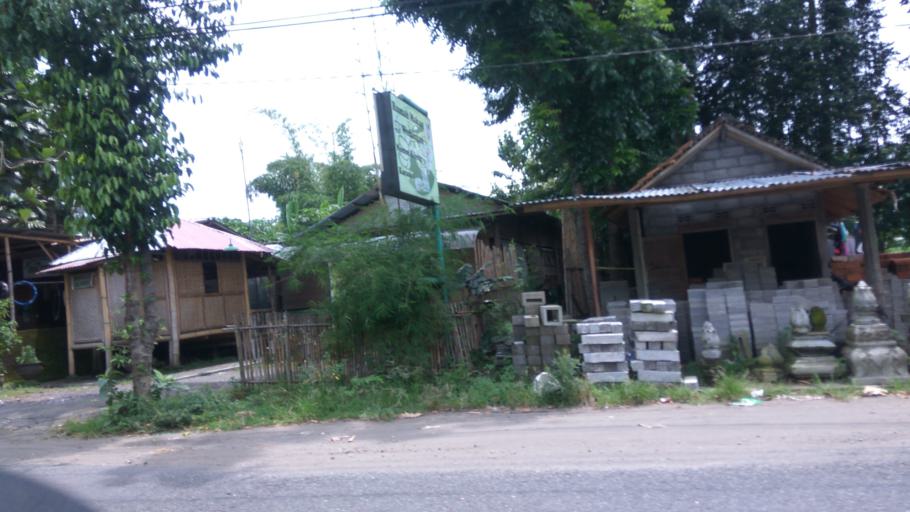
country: ID
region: Daerah Istimewa Yogyakarta
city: Depok
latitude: -7.7485
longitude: 110.4195
